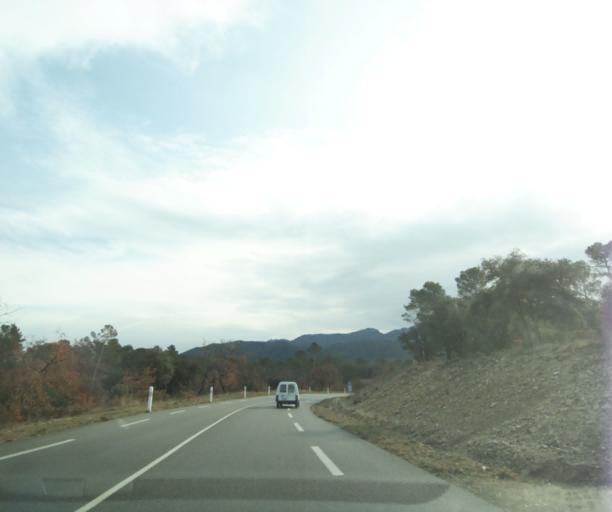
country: FR
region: Provence-Alpes-Cote d'Azur
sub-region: Departement du Var
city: Tourves
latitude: 43.4009
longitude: 5.9619
